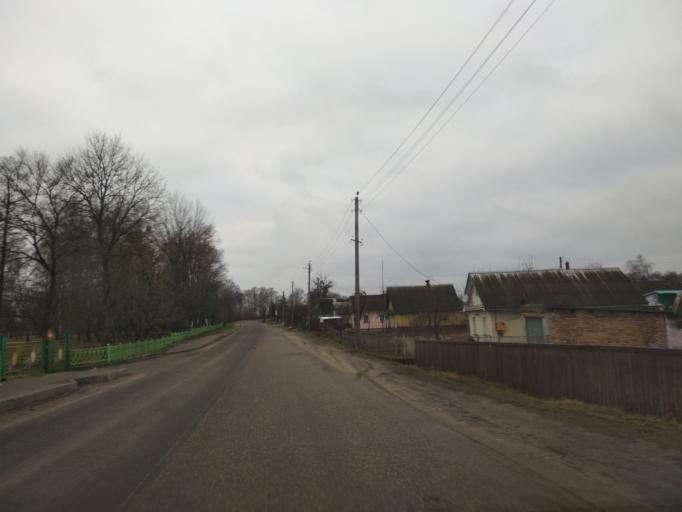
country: BY
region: Minsk
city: Mar''ina Horka
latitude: 53.5256
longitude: 28.1388
